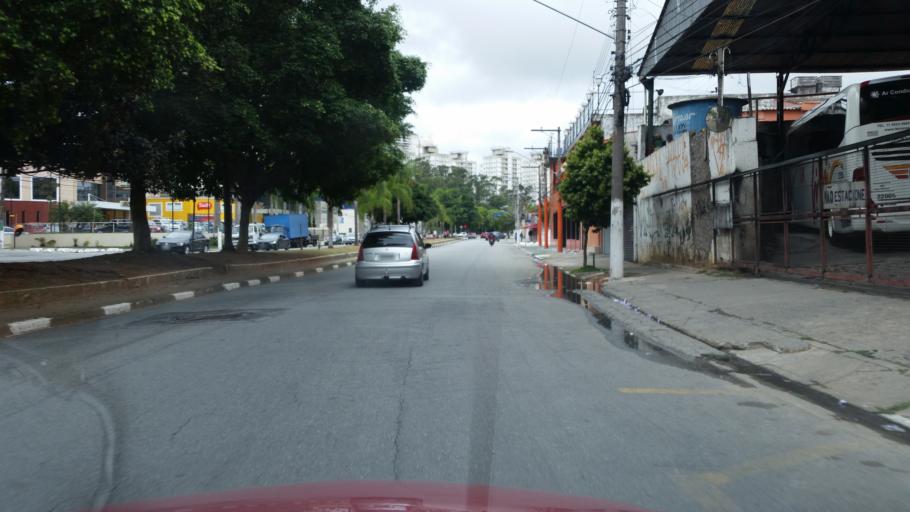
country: BR
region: Sao Paulo
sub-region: Diadema
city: Diadema
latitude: -23.6620
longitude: -46.6901
